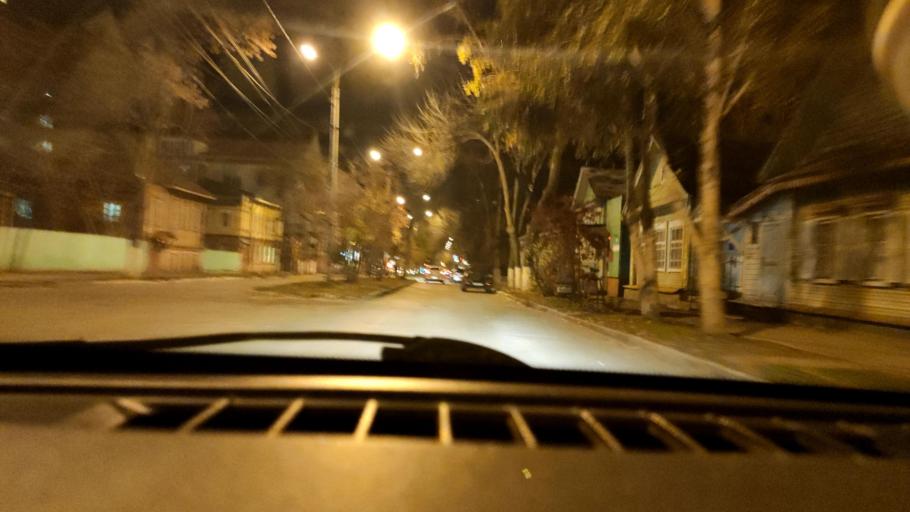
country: RU
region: Samara
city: Samara
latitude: 53.1929
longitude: 50.1104
